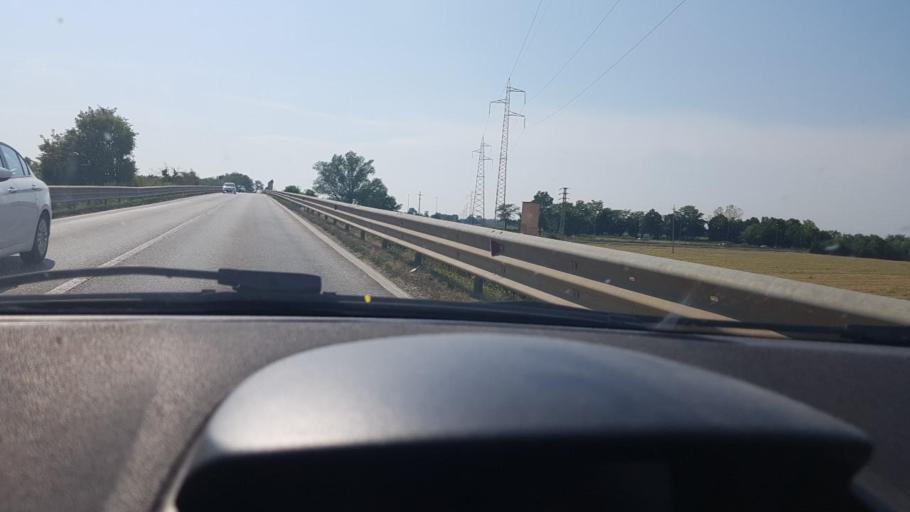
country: IT
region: Friuli Venezia Giulia
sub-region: Provincia di Udine
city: Bagnaria Arsa
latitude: 45.8989
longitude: 13.2892
